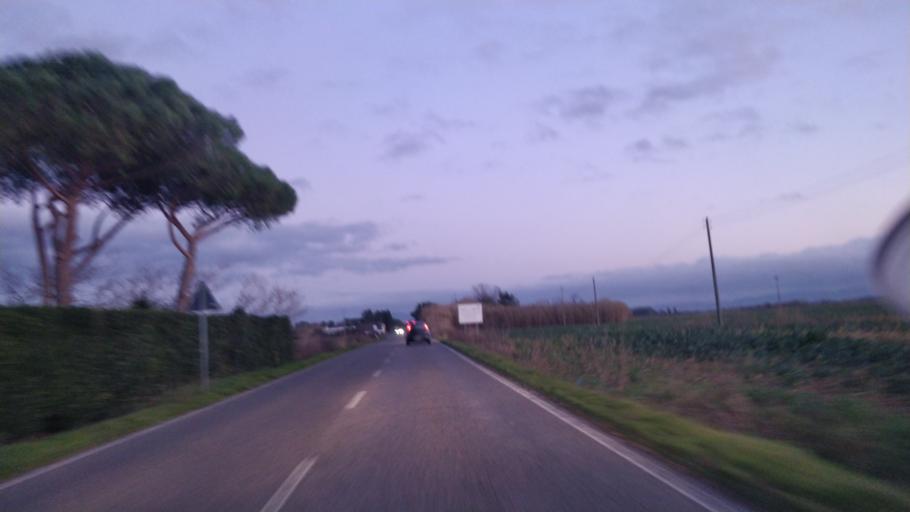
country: IT
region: Tuscany
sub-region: Provincia di Livorno
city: Vada
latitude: 43.3451
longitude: 10.4704
